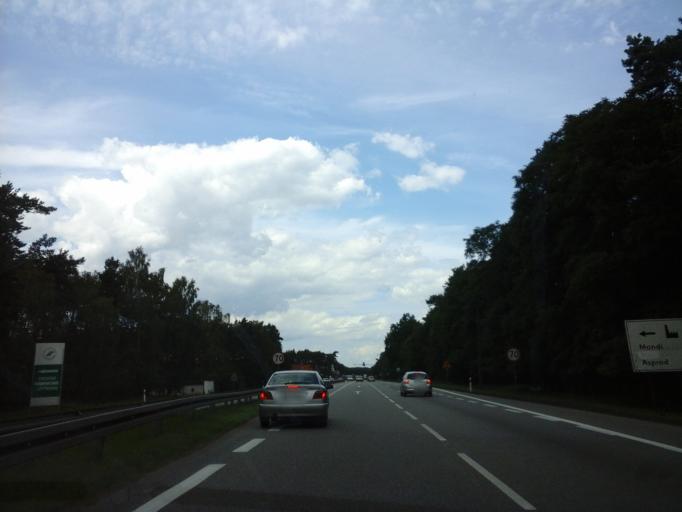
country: PL
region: West Pomeranian Voivodeship
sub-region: Powiat goleniowski
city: Goleniow
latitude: 53.4591
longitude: 14.7882
